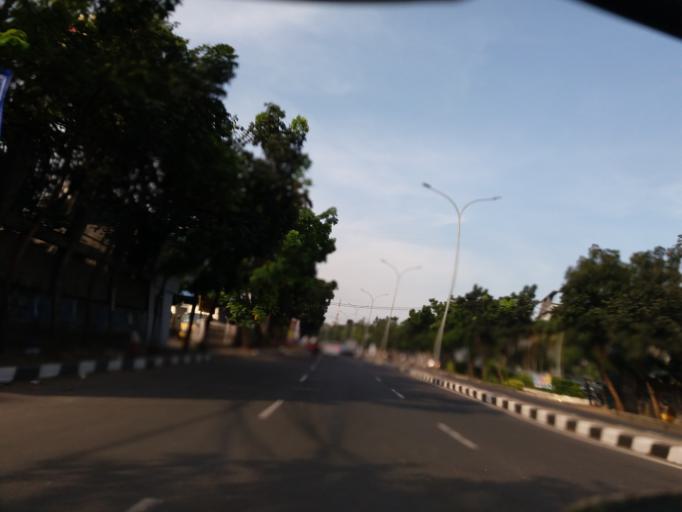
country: ID
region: West Java
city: Bandung
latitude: -6.9493
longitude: 107.6283
